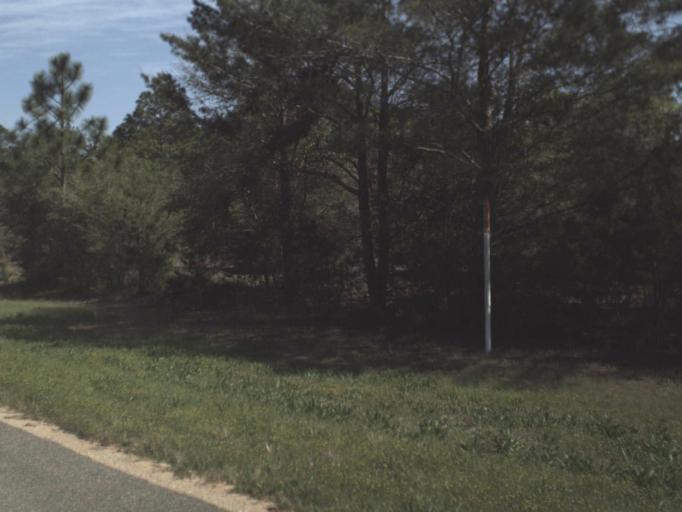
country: US
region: Florida
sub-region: Okaloosa County
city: Crestview
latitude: 30.7435
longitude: -86.4038
